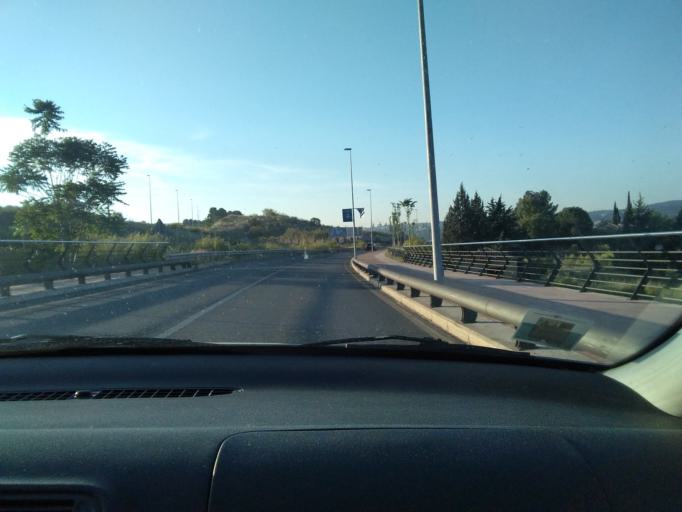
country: ES
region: Castille-La Mancha
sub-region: Province of Toledo
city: Toledo
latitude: 39.8840
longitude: -4.0539
